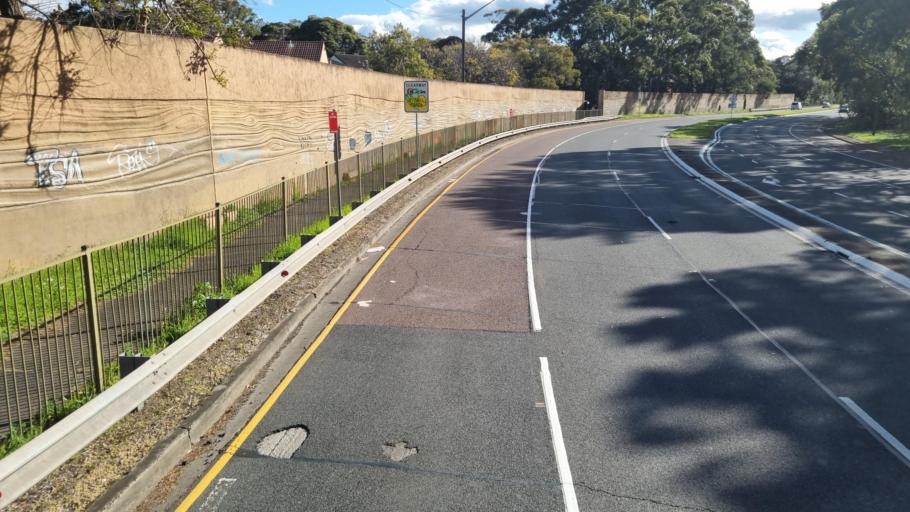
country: AU
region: New South Wales
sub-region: Manly Vale
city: Balgowlah
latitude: -33.7886
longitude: 151.2654
